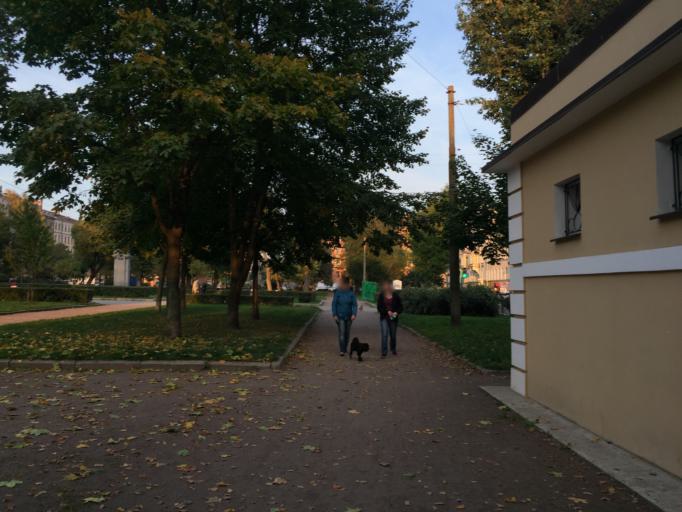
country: RU
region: St.-Petersburg
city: Admiralteisky
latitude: 59.9180
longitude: 30.2885
